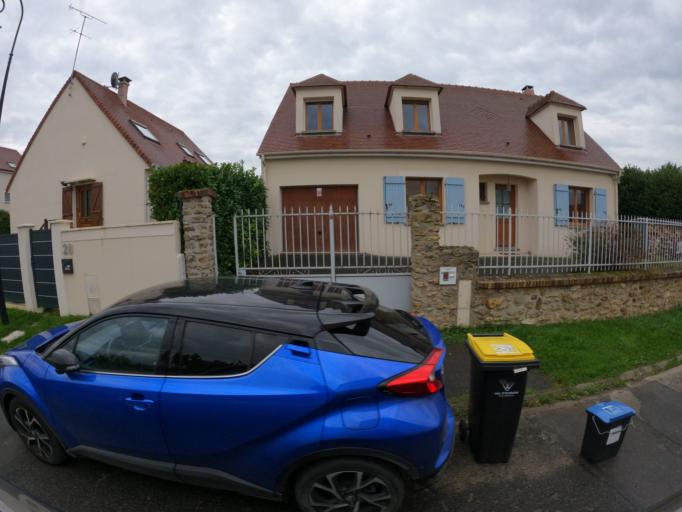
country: FR
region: Ile-de-France
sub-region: Departement de Seine-et-Marne
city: Villeneuve-le-Comte
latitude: 48.8147
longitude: 2.8329
